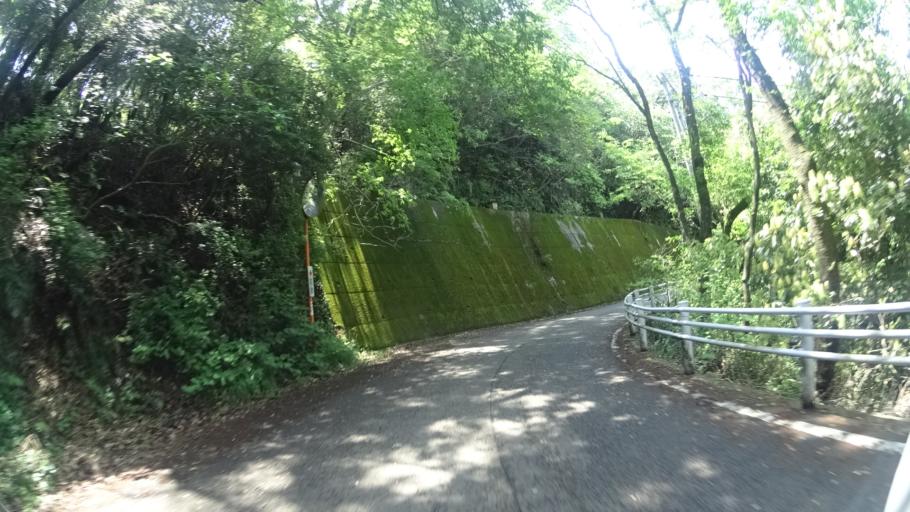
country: JP
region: Tokushima
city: Tokushima-shi
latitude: 34.0672
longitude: 134.5146
